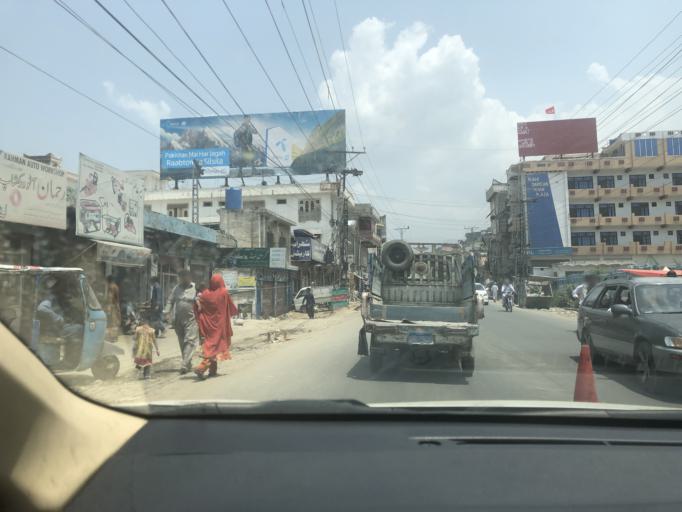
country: PK
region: Khyber Pakhtunkhwa
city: Mingora
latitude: 34.7695
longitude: 72.3389
